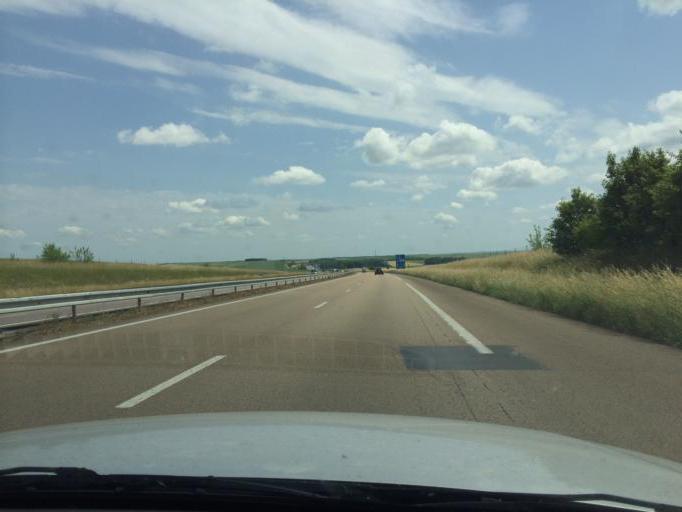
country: FR
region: Champagne-Ardenne
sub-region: Departement de la Marne
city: Mourmelon-le-Grand
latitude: 49.0723
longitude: 4.2672
